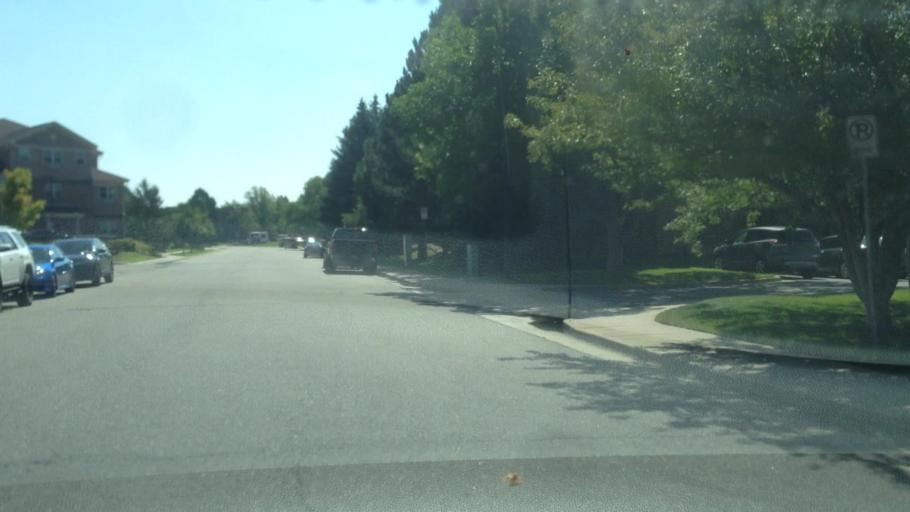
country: US
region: Colorado
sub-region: Adams County
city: Aurora
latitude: 39.6781
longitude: -104.8234
